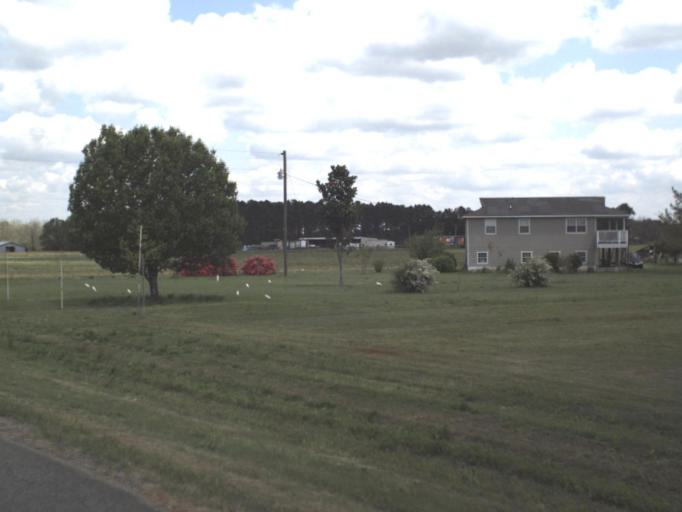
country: US
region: Florida
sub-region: Okaloosa County
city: Crestview
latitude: 30.8376
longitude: -86.6753
